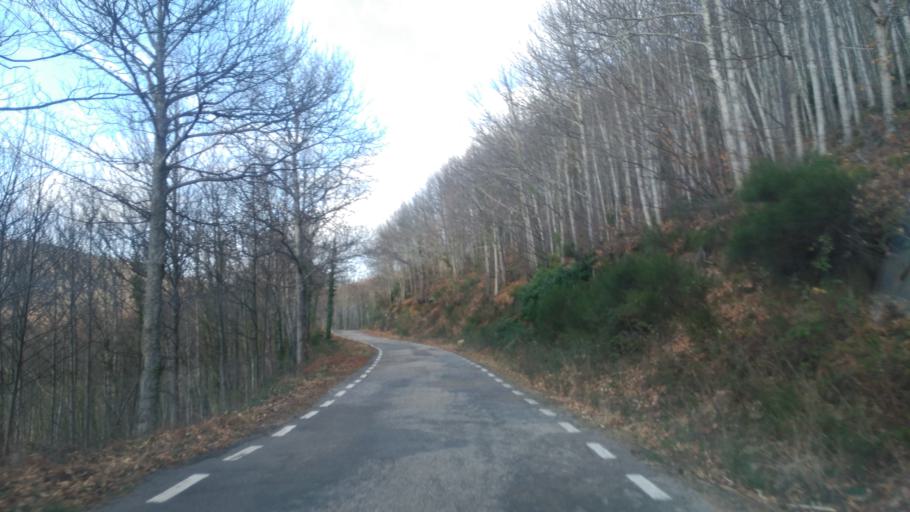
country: ES
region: Castille and Leon
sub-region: Provincia de Salamanca
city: San Martin del Castanar
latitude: 40.5232
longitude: -6.0507
